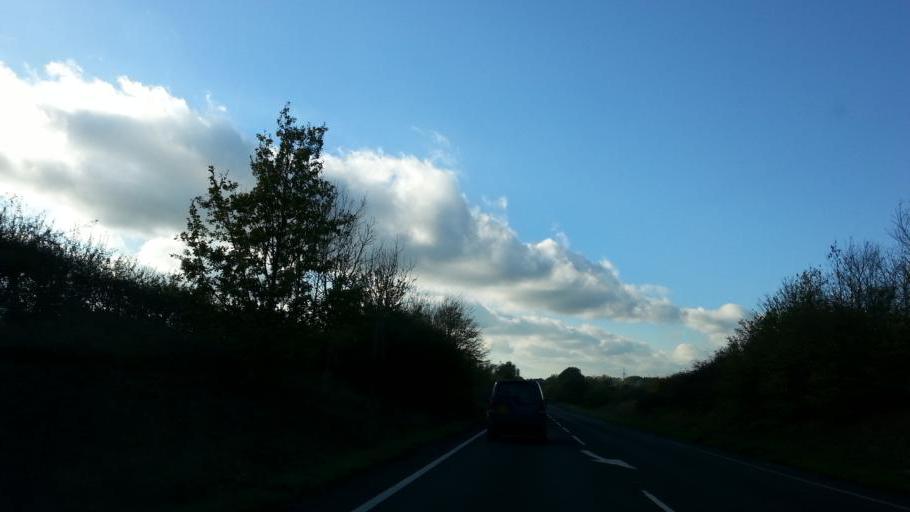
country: GB
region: England
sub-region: Norfolk
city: Diss
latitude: 52.3630
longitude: 1.1667
